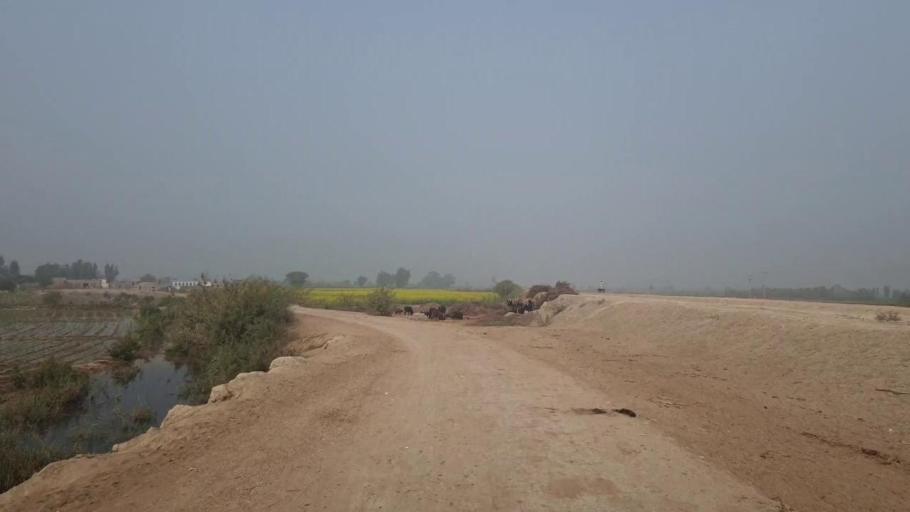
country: PK
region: Sindh
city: Bhit Shah
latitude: 25.8179
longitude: 68.5690
